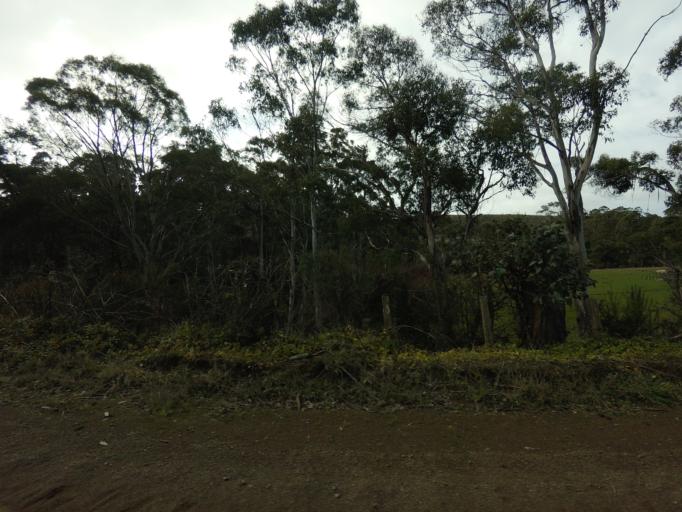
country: AU
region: Tasmania
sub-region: Derwent Valley
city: New Norfolk
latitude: -42.7533
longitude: 146.8759
